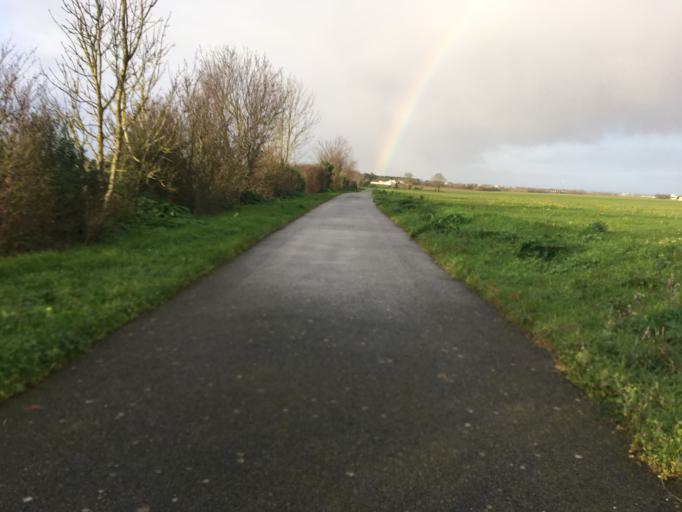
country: FR
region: Poitou-Charentes
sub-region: Departement de la Charente-Maritime
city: Nieul-sur-Mer
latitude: 46.1971
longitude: -1.1616
